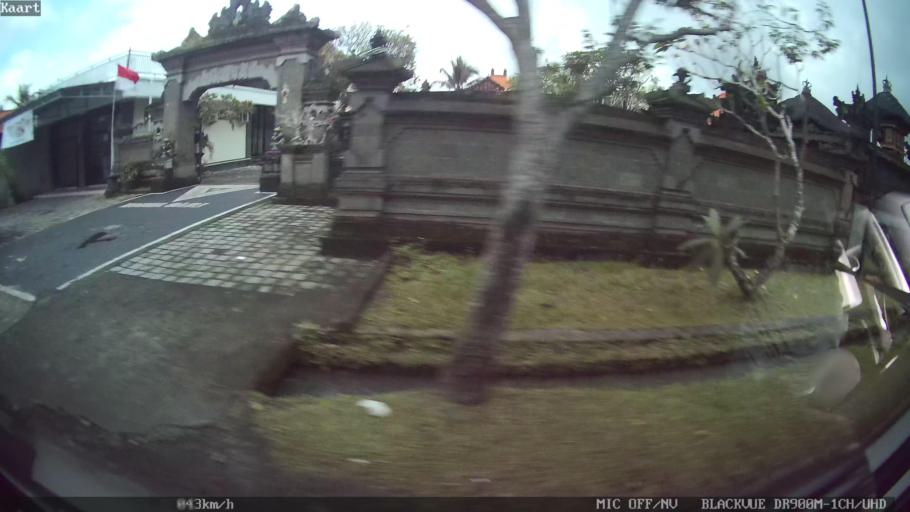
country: ID
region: Bali
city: Banjar Keraman
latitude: -8.5404
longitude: 115.2143
